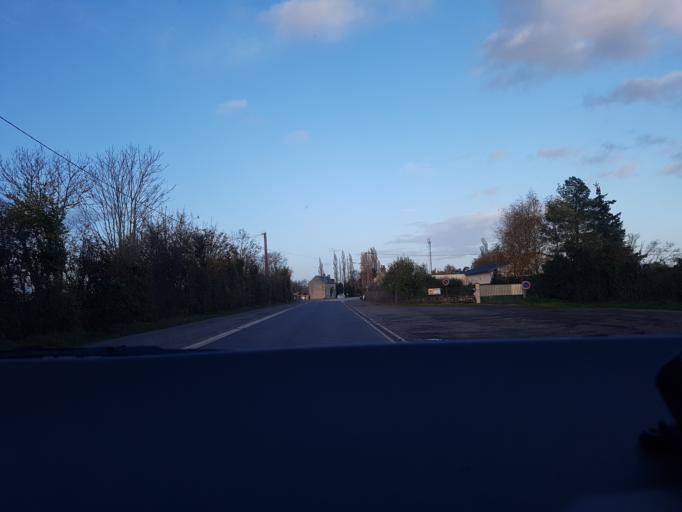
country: FR
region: Lower Normandy
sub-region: Departement du Calvados
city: Dives-sur-Mer
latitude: 49.2110
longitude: -0.1143
